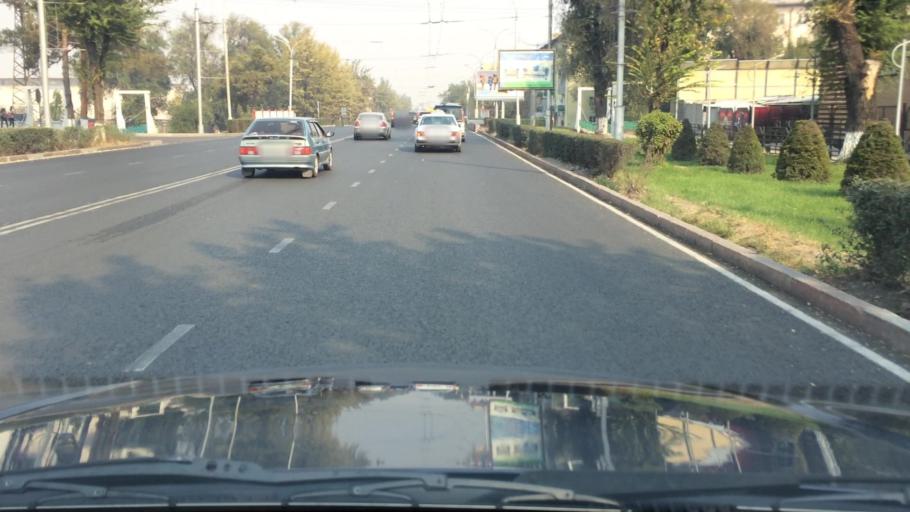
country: KG
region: Chuy
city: Bishkek
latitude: 42.8555
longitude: 74.5868
